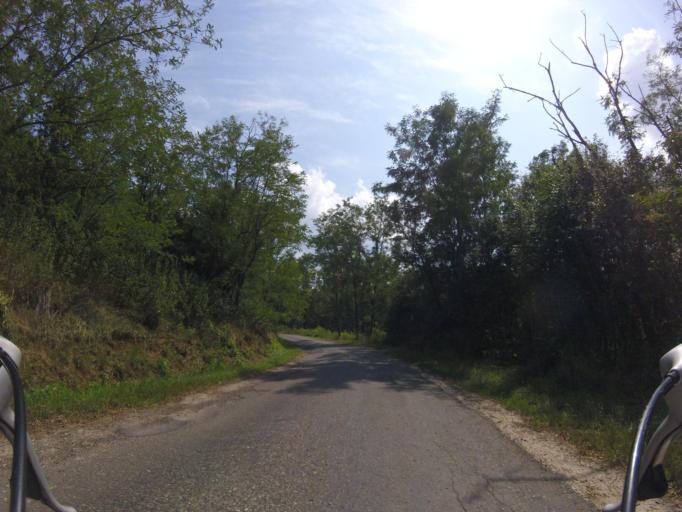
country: SK
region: Nitriansky
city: Sahy
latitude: 48.0012
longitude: 18.8214
